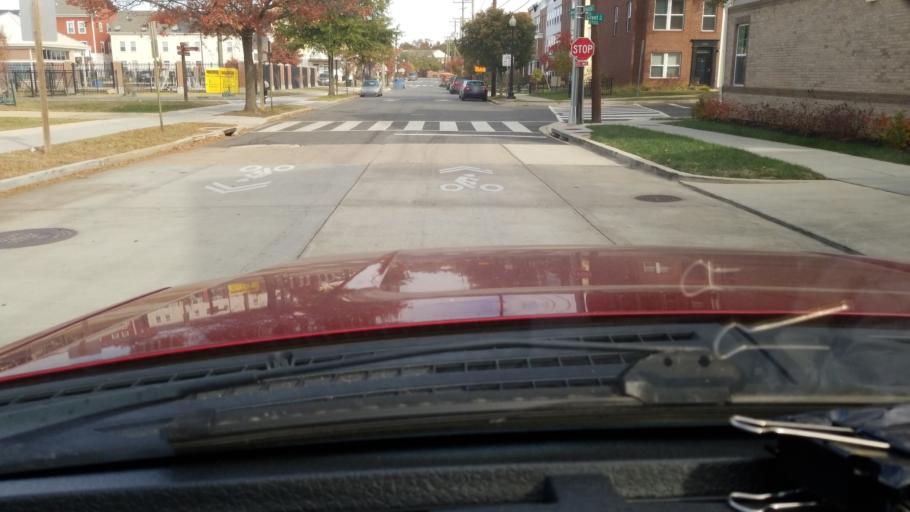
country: US
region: Maryland
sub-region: Prince George's County
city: Colmar Manor
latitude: 38.9011
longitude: -76.9517
